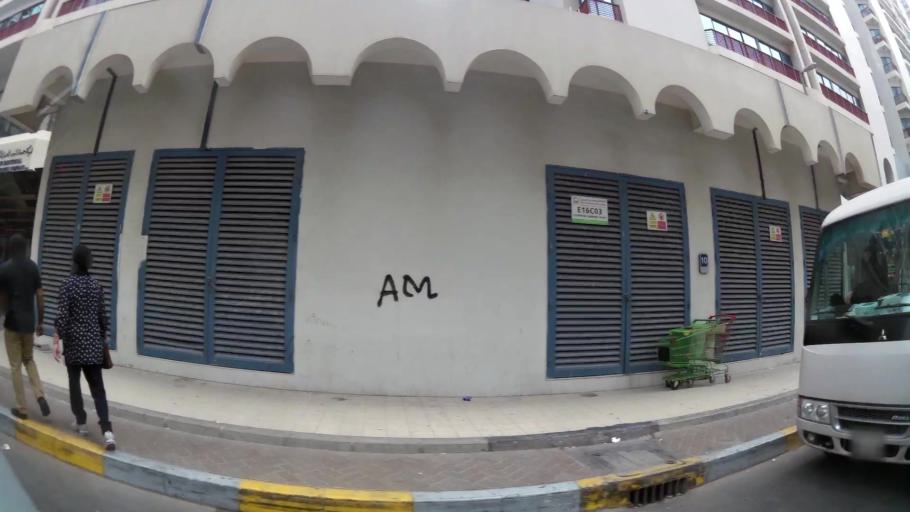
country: AE
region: Abu Dhabi
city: Abu Dhabi
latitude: 24.4939
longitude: 54.3792
